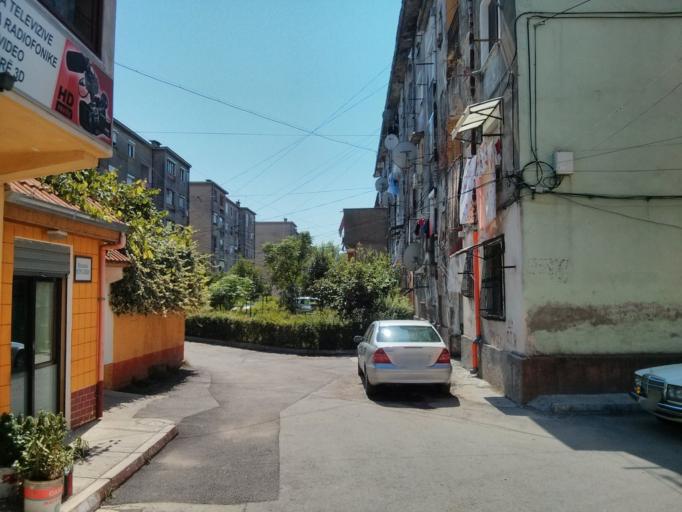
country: AL
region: Shkoder
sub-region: Rrethi i Shkodres
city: Shkoder
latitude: 42.0681
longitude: 19.5137
